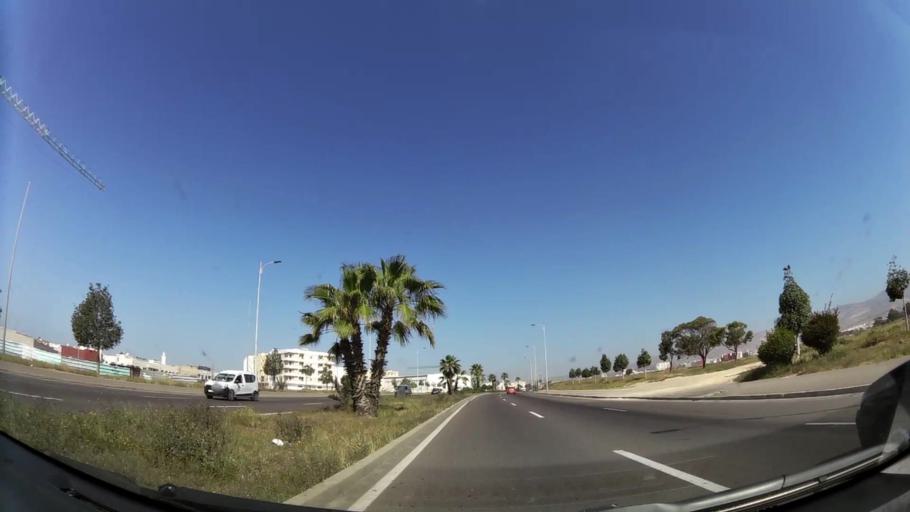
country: MA
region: Oued ed Dahab-Lagouira
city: Dakhla
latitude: 30.4183
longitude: -9.5508
